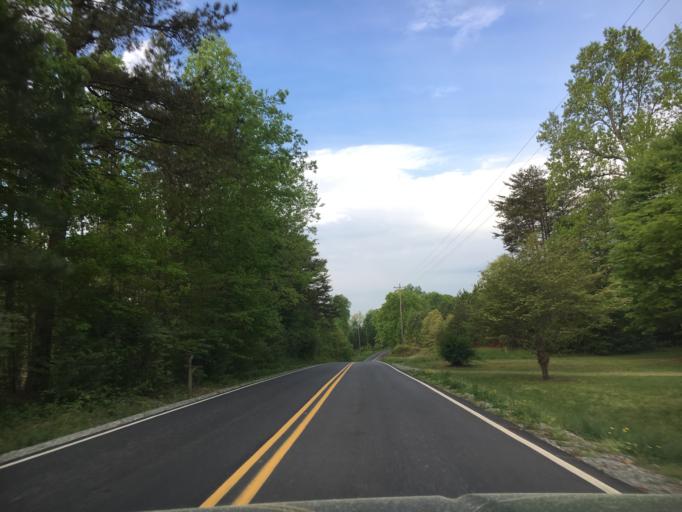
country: US
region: Virginia
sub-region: Halifax County
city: Halifax
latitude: 36.8918
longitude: -78.8341
